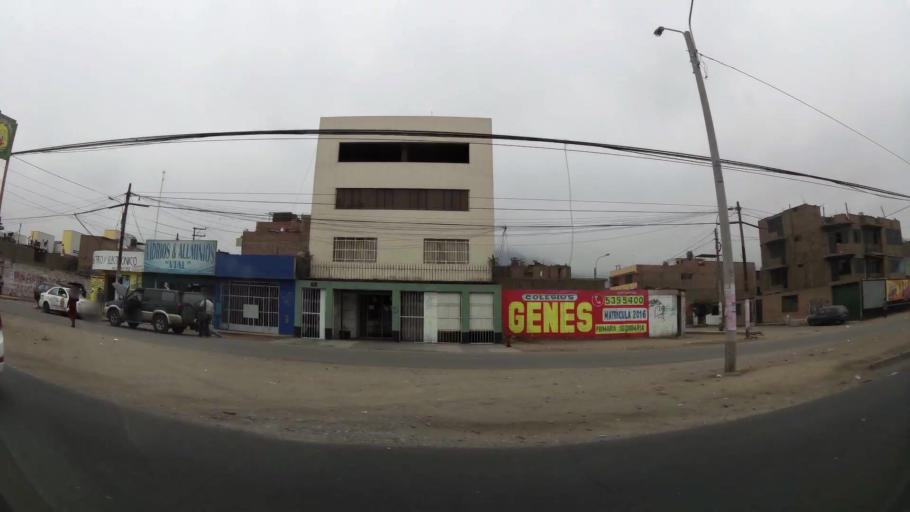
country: PE
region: Lima
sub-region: Lima
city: Independencia
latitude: -11.9493
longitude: -77.0602
